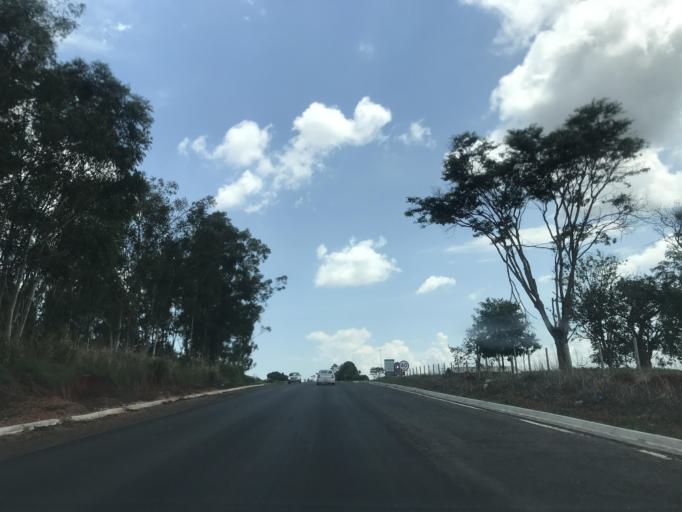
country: BR
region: Goias
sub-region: Bela Vista De Goias
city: Bela Vista de Goias
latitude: -17.0671
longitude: -48.6575
